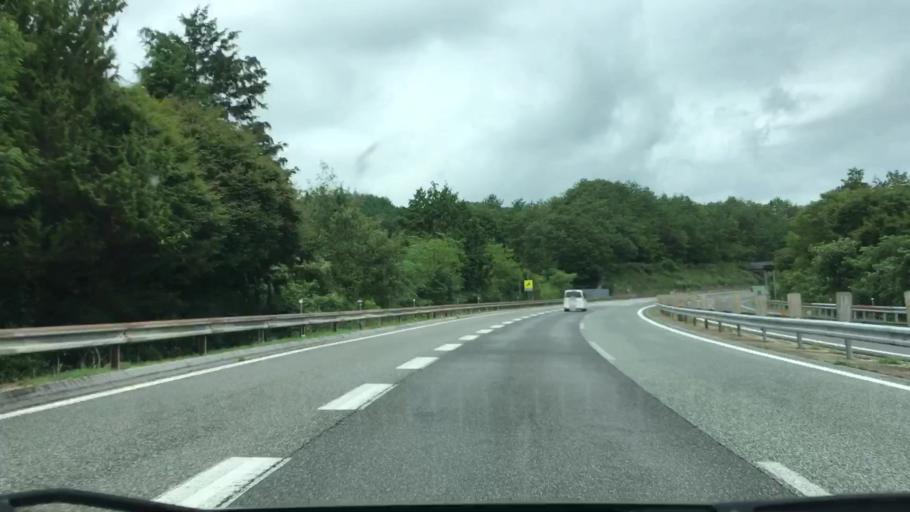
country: JP
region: Hiroshima
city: Miyoshi
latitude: 34.7528
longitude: 132.7643
